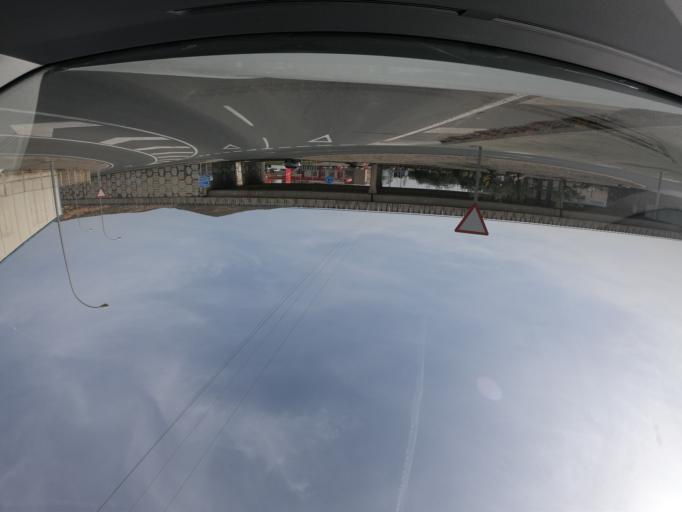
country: ES
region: La Rioja
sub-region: Provincia de La Rioja
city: Logrono
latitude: 42.4722
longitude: -2.4156
